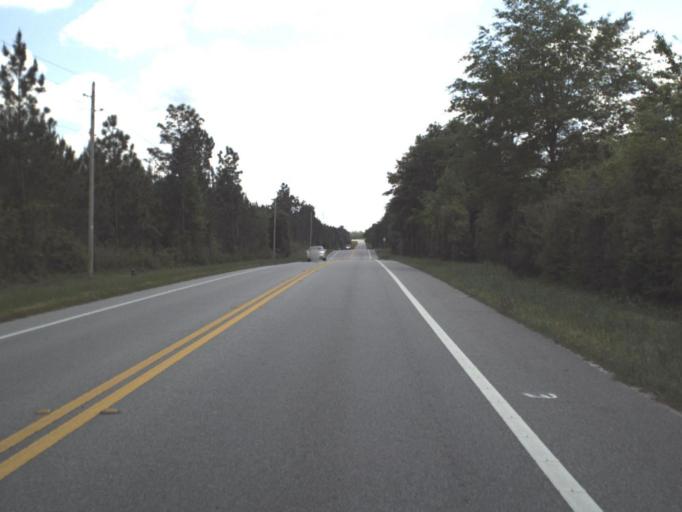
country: US
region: Florida
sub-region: Escambia County
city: Molino
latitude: 30.7609
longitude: -87.3819
